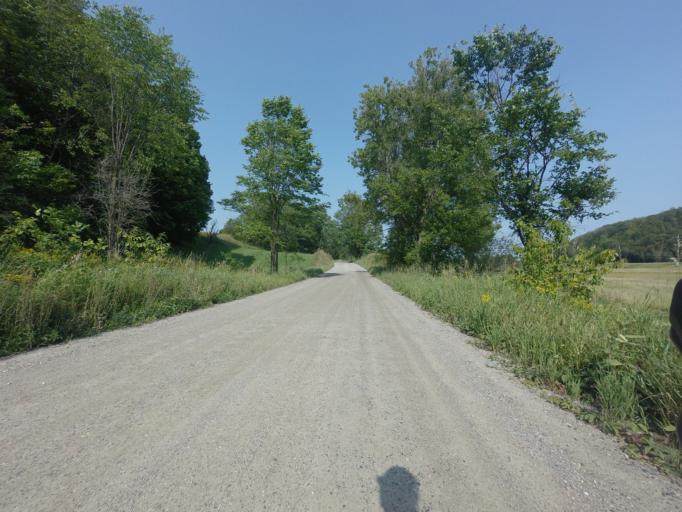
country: CA
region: Ontario
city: Skatepark
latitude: 44.7549
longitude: -76.8248
